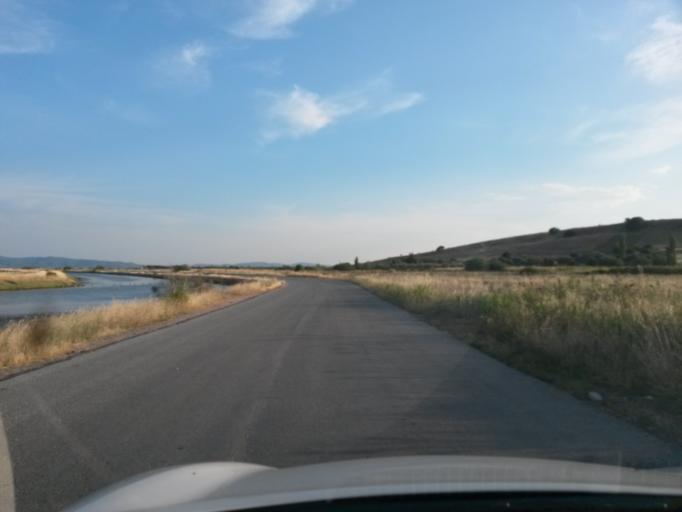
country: GR
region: North Aegean
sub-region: Nomos Lesvou
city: Kalloni
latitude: 39.2255
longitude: 26.2425
